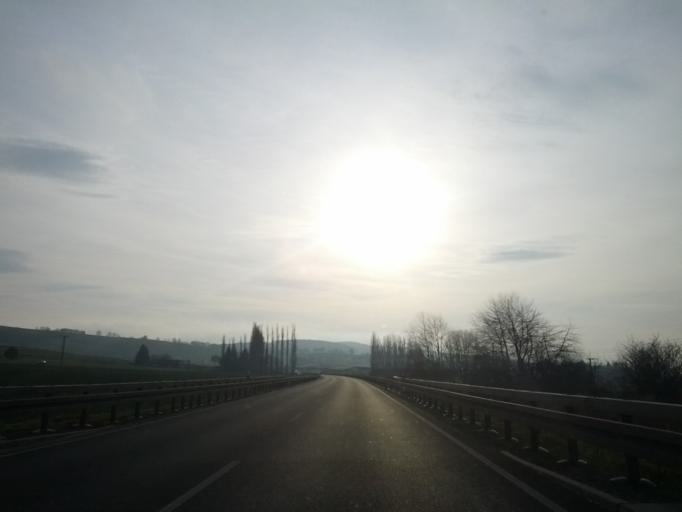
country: DE
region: Thuringia
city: Fambach
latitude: 50.7344
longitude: 10.3615
